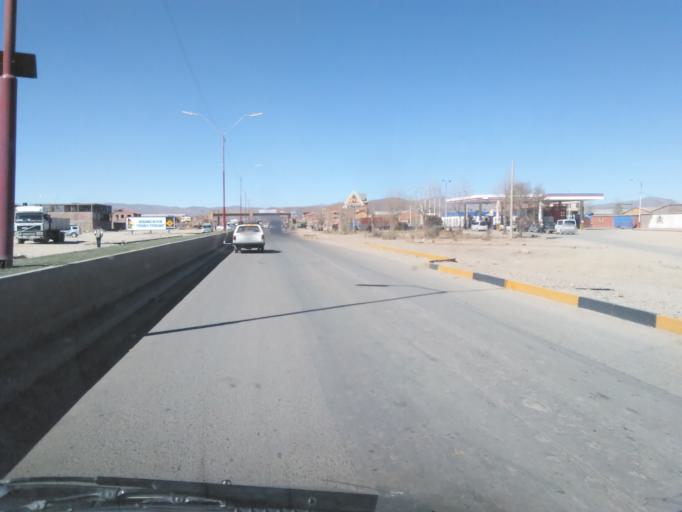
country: BO
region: Oruro
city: Oruro
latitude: -17.9726
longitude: -67.0881
